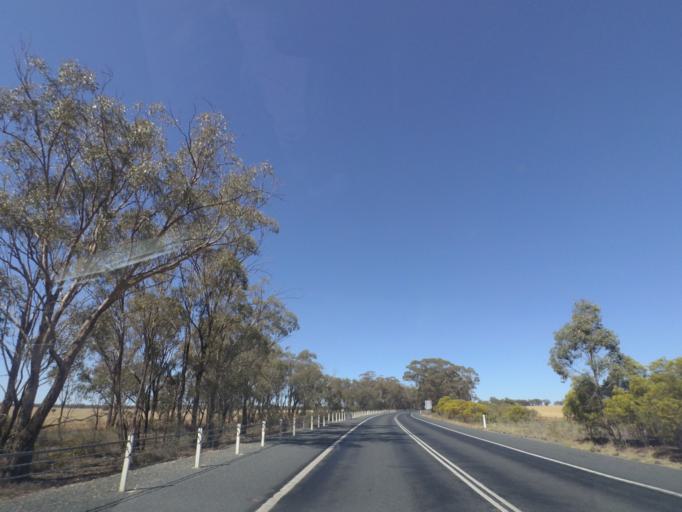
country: AU
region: New South Wales
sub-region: Bland
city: West Wyalong
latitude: -34.1134
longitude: 147.1381
